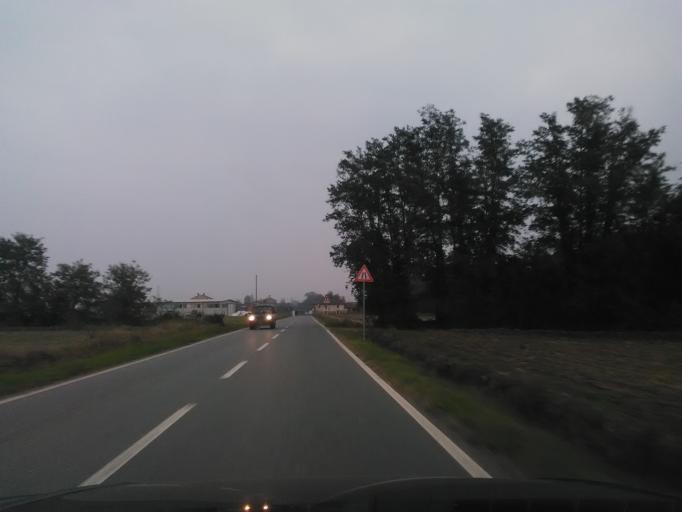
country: IT
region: Piedmont
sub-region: Provincia di Vercelli
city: Alice Castello
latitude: 45.3622
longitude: 8.1116
